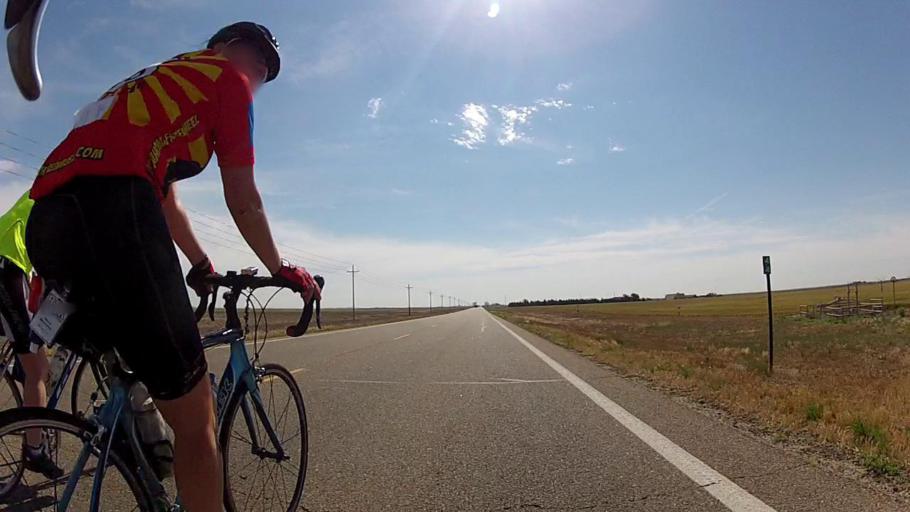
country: US
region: Kansas
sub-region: Grant County
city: Ulysses
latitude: 37.5617
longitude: -101.2891
